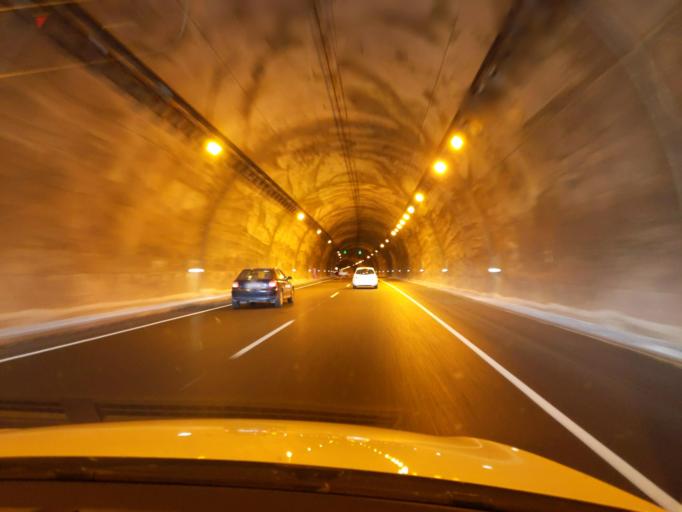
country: ES
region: Navarre
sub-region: Provincia de Navarra
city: Uterga
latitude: 42.7336
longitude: -1.7532
